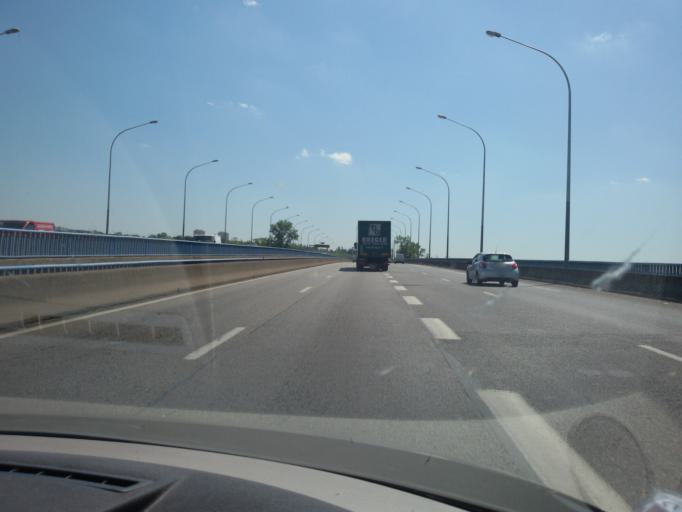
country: FR
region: Rhone-Alpes
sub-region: Departement du Rhone
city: Pierre-Benite
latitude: 45.6965
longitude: 4.8384
